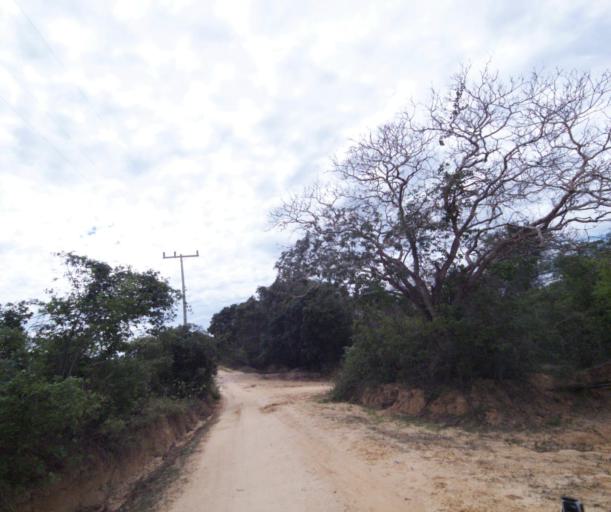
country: BR
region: Bahia
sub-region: Carinhanha
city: Carinhanha
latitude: -14.2543
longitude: -44.3631
